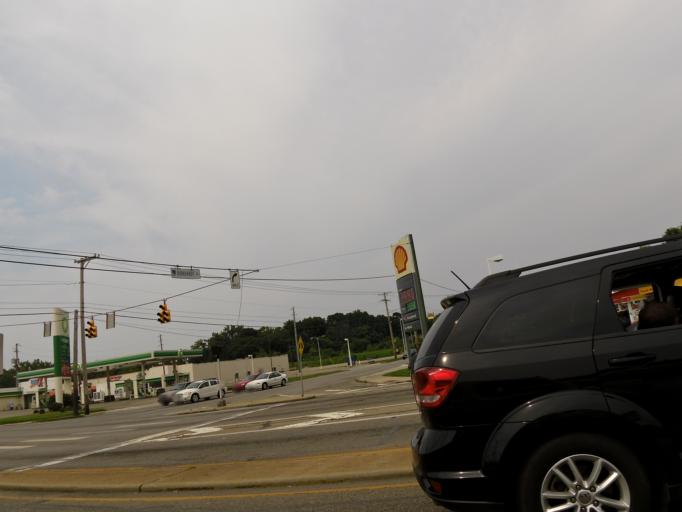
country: US
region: Ohio
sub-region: Montgomery County
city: Riverside
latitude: 39.7596
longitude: -84.1203
